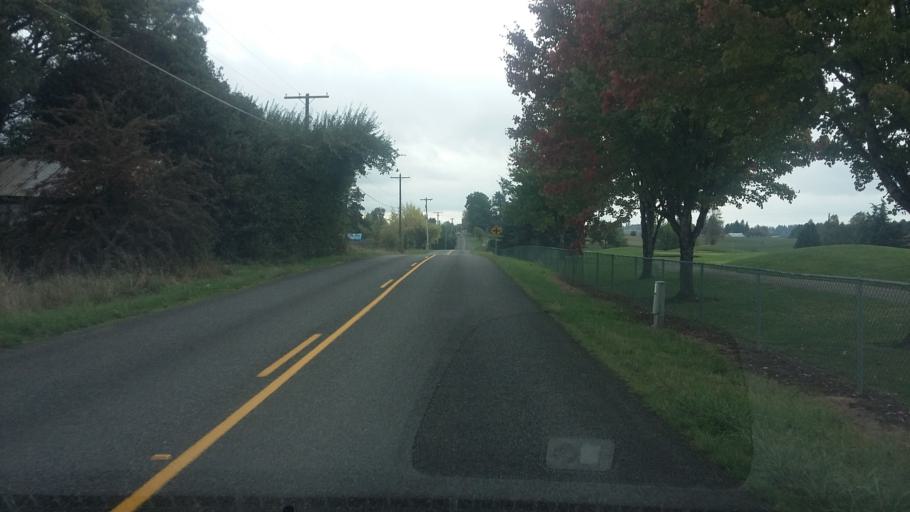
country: US
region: Washington
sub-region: Clark County
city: La Center
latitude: 45.8324
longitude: -122.6825
